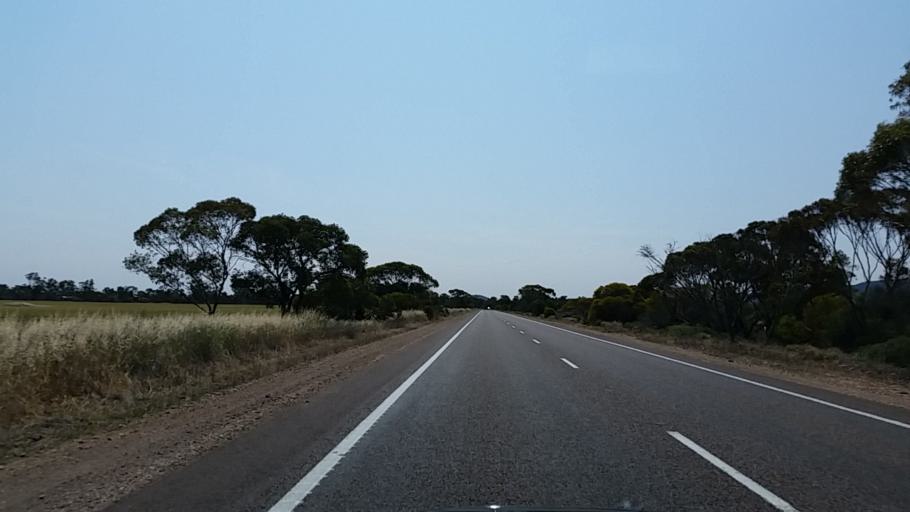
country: AU
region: South Australia
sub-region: Port Pirie City and Dists
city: Port Pirie
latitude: -32.8639
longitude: 137.9822
